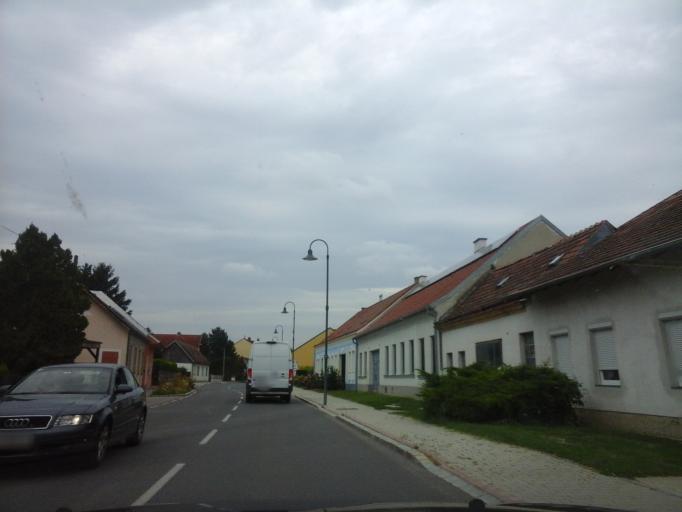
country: AT
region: Lower Austria
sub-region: Politischer Bezirk Ganserndorf
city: Mannsdorf an der Donau
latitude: 48.1521
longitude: 16.6657
